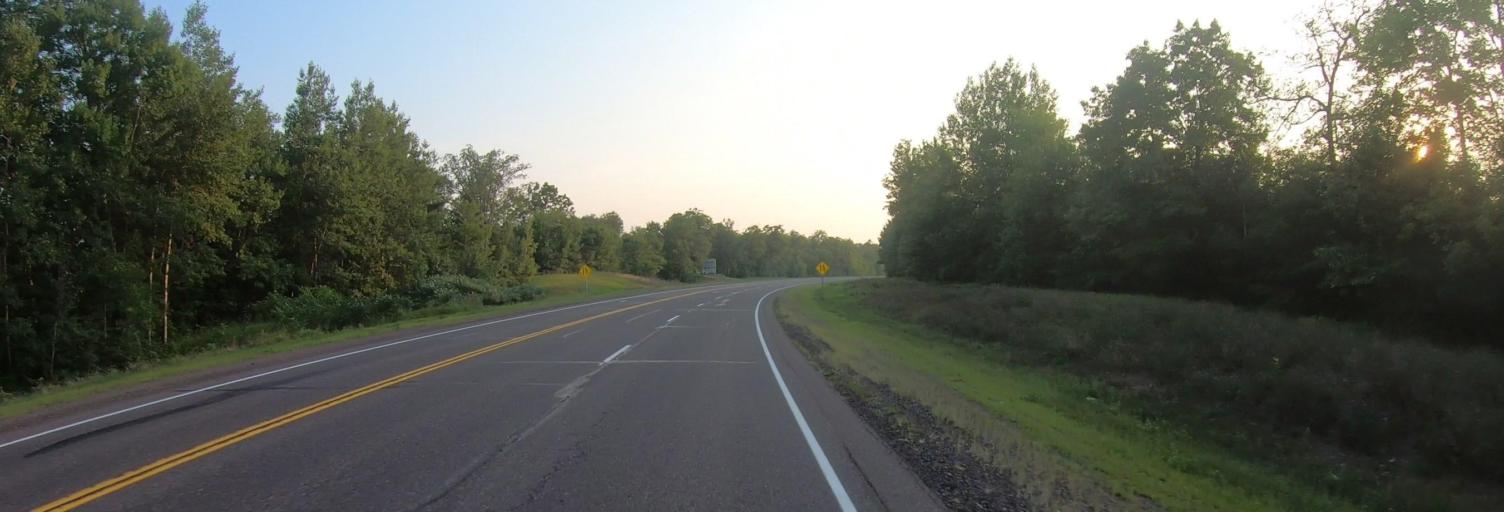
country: US
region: Wisconsin
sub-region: Burnett County
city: Siren
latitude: 45.7780
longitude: -92.4338
